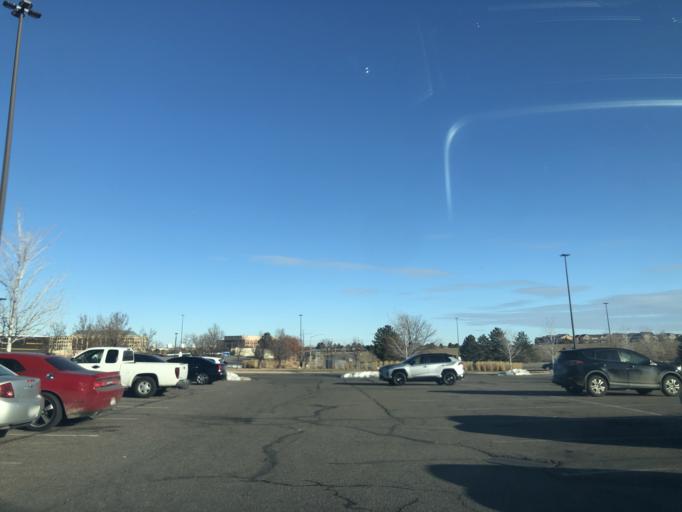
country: US
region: Colorado
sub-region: Adams County
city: Aurora
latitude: 39.7079
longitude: -104.8219
